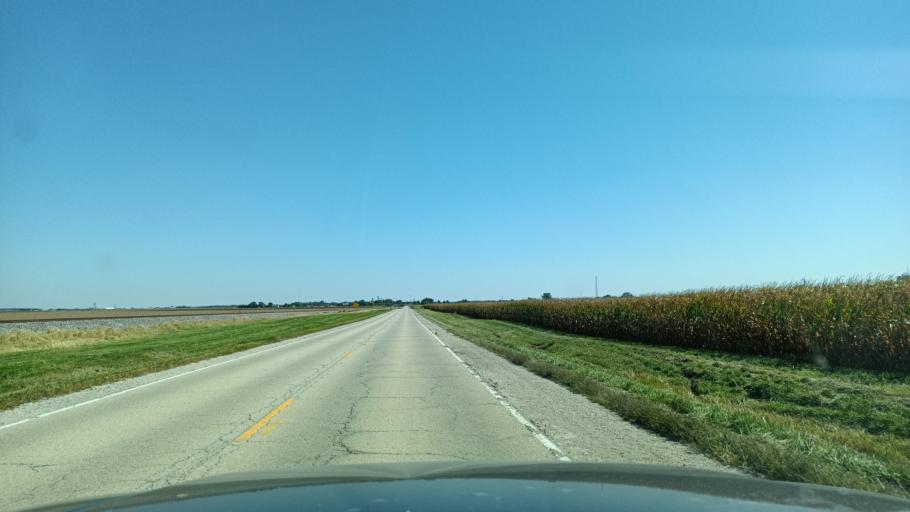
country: US
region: Illinois
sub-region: Tazewell County
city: Mackinaw
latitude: 40.6264
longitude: -89.3201
